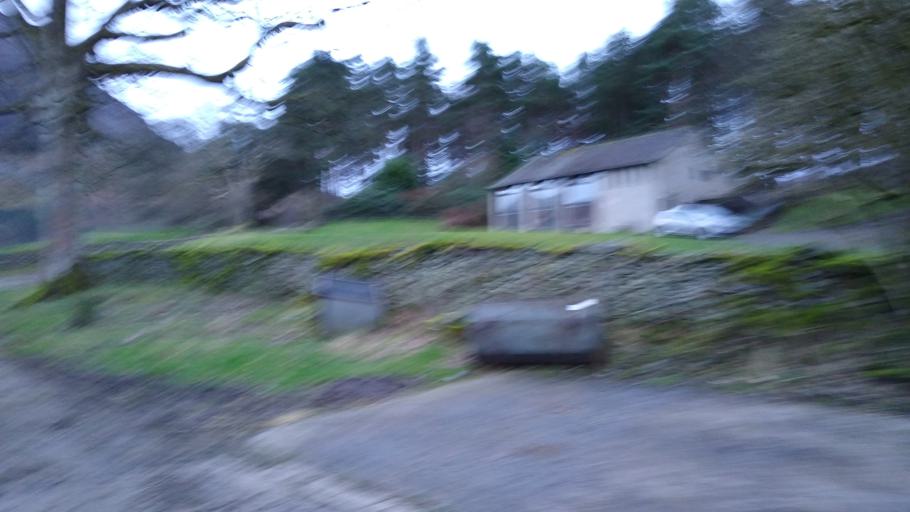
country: GB
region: England
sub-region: Cumbria
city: Cockermouth
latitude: 54.5740
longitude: -3.3315
